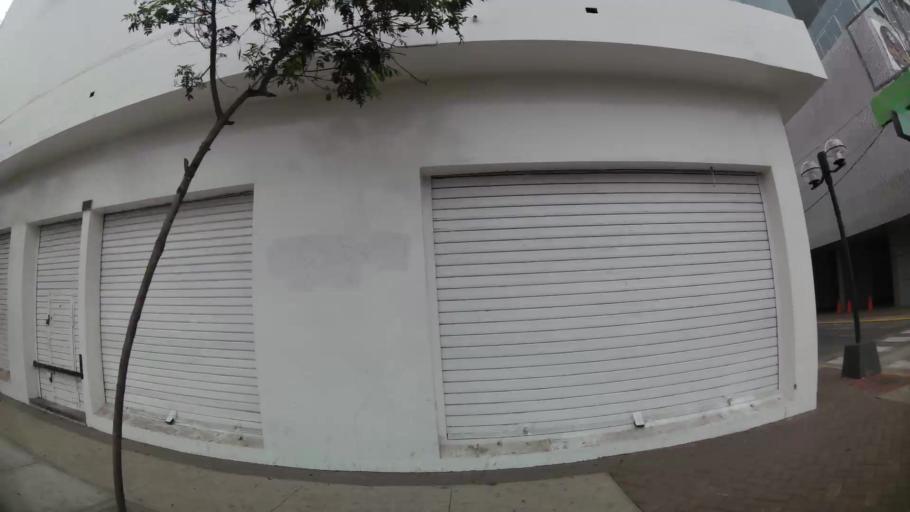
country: PE
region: Lima
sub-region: Lima
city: San Isidro
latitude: -12.1184
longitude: -77.0264
